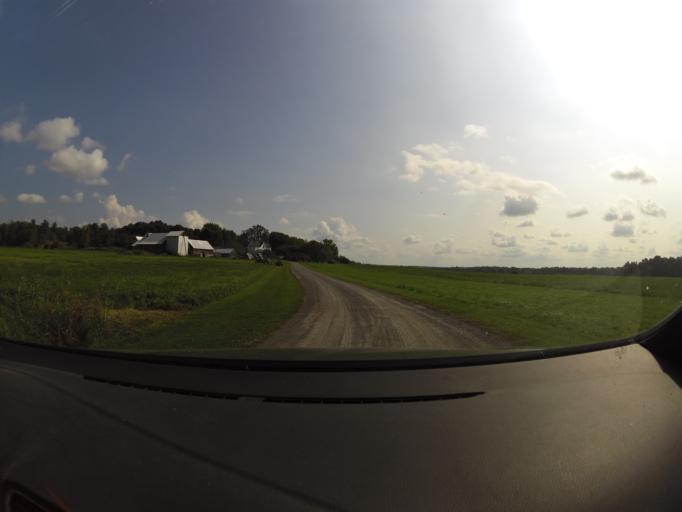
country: CA
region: Ontario
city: Arnprior
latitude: 45.4065
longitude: -76.2422
